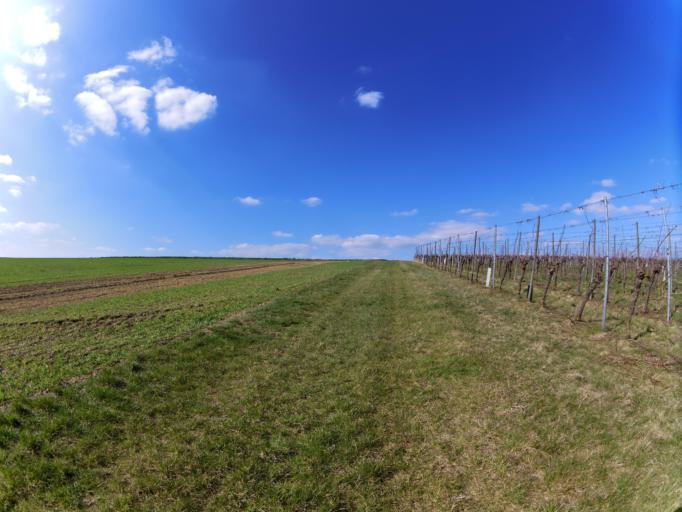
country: DE
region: Bavaria
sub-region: Regierungsbezirk Unterfranken
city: Nordheim
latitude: 49.8347
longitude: 10.1693
